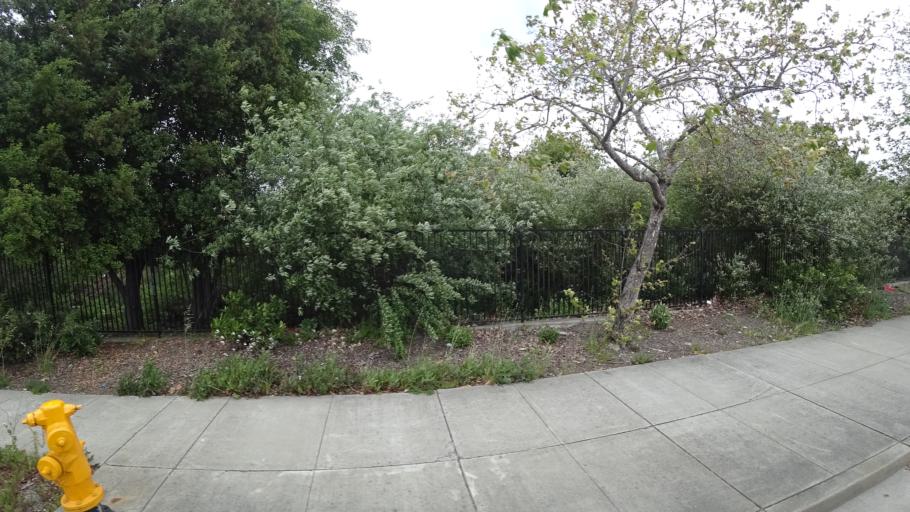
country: US
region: California
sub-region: Alameda County
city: San Lorenzo
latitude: 37.6620
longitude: -122.1183
